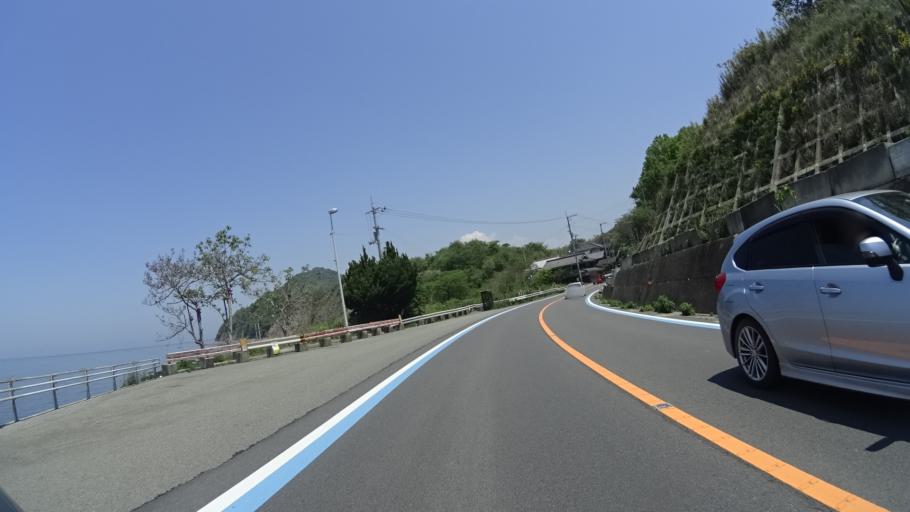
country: JP
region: Ehime
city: Iyo
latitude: 33.7069
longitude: 132.6611
